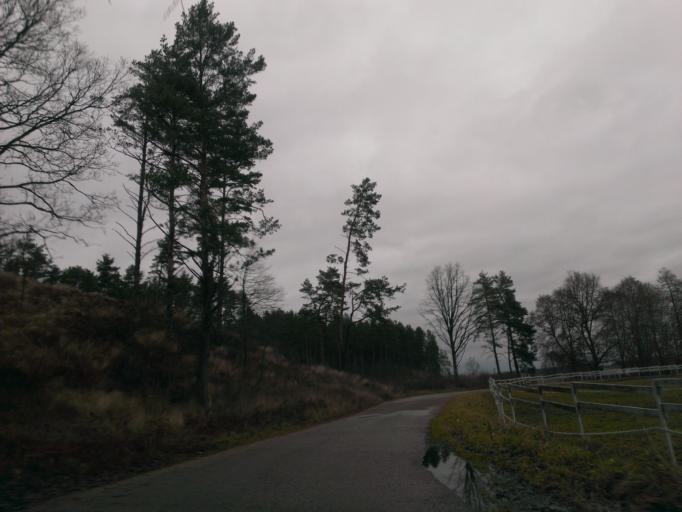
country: LV
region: Adazi
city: Adazi
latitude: 57.0602
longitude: 24.3546
